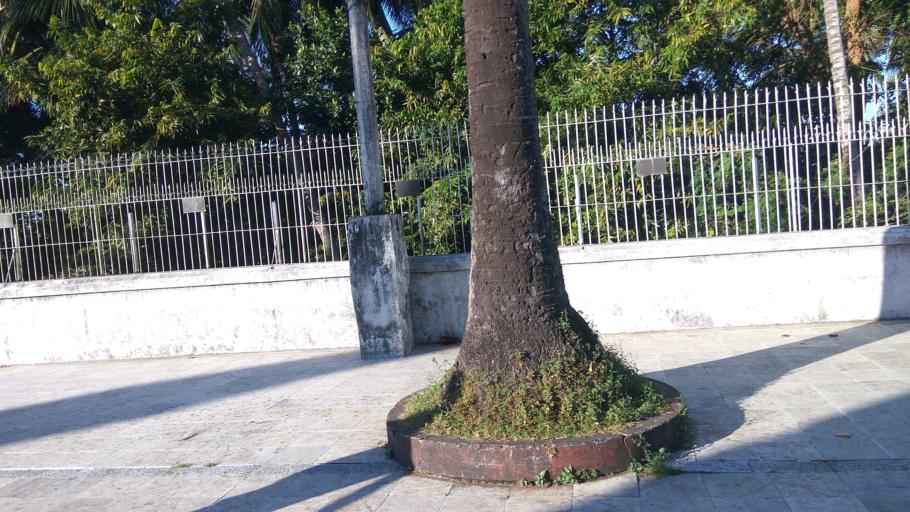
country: MM
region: Yangon
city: Yangon
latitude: 16.7994
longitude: 96.1484
